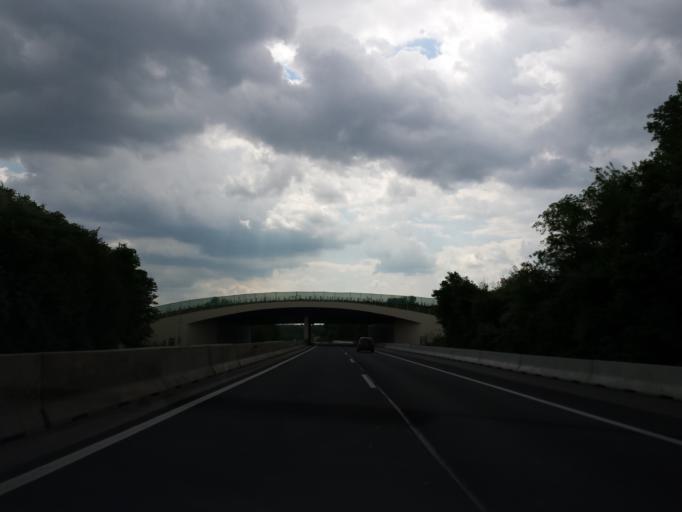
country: AT
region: Lower Austria
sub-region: Politischer Bezirk Ganserndorf
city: Orth an der Donau
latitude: 48.0734
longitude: 16.6835
